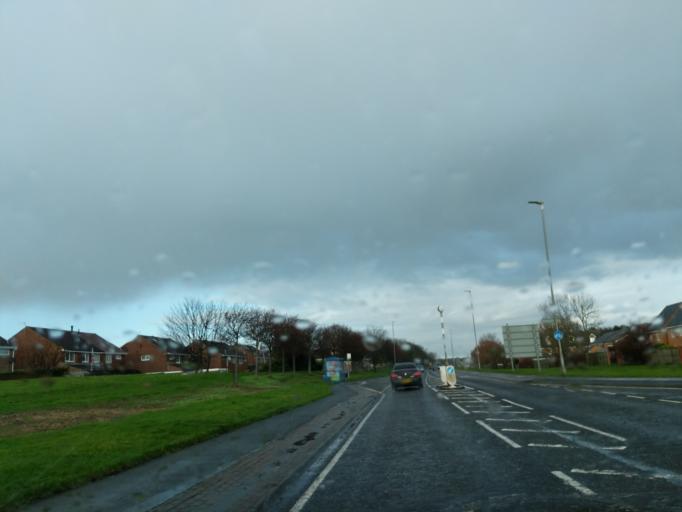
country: GB
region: England
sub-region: Northumberland
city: Blyth
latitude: 55.1108
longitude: -1.5043
